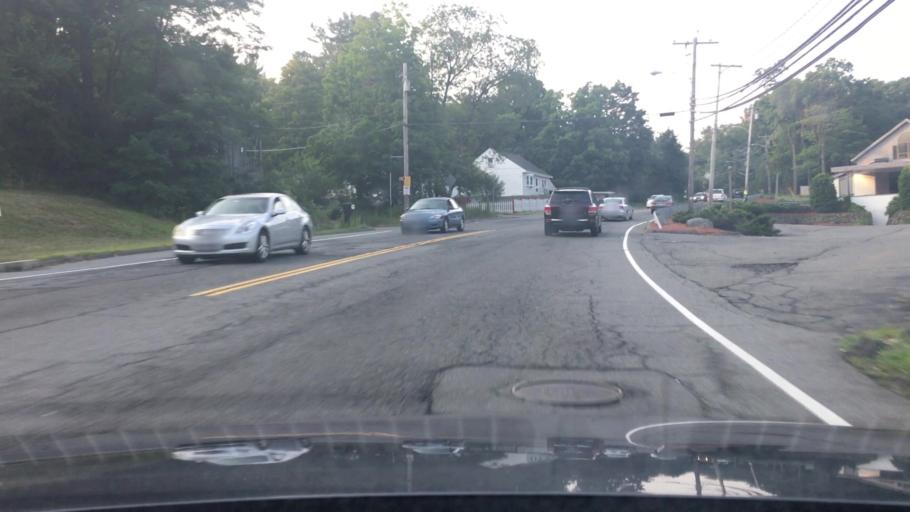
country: US
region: Massachusetts
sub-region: Essex County
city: Saugus
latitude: 42.4871
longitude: -71.0145
